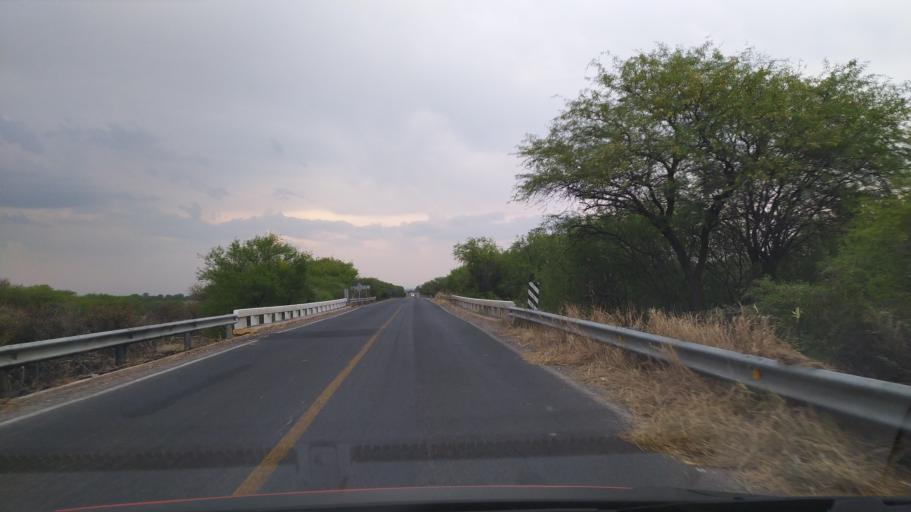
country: MX
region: Guanajuato
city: Ciudad Manuel Doblado
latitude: 20.7527
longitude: -101.9226
